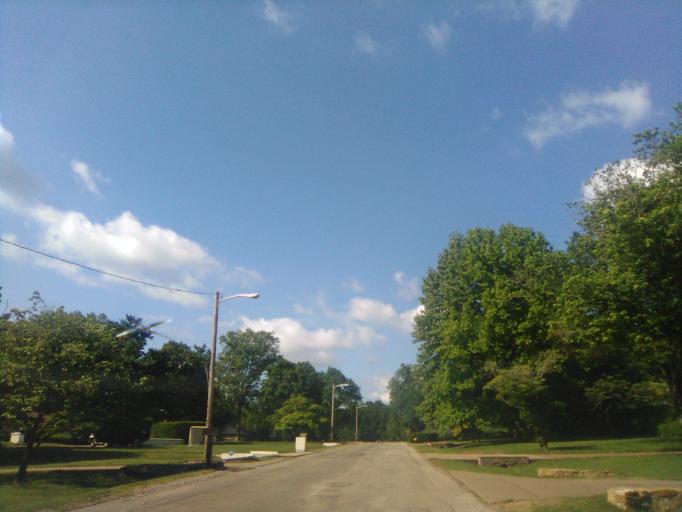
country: US
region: Tennessee
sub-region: Davidson County
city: Belle Meade
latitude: 36.1114
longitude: -86.8697
